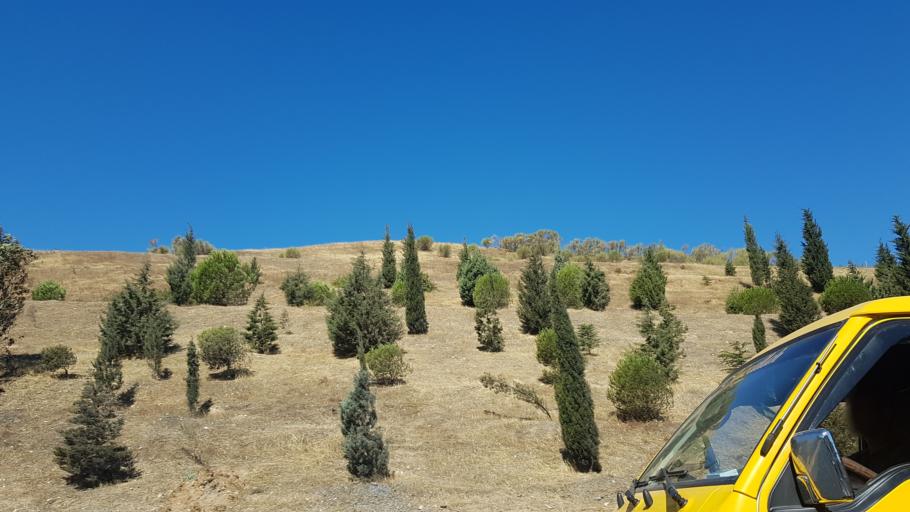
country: TR
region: Izmir
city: Buca
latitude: 38.4004
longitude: 27.2297
